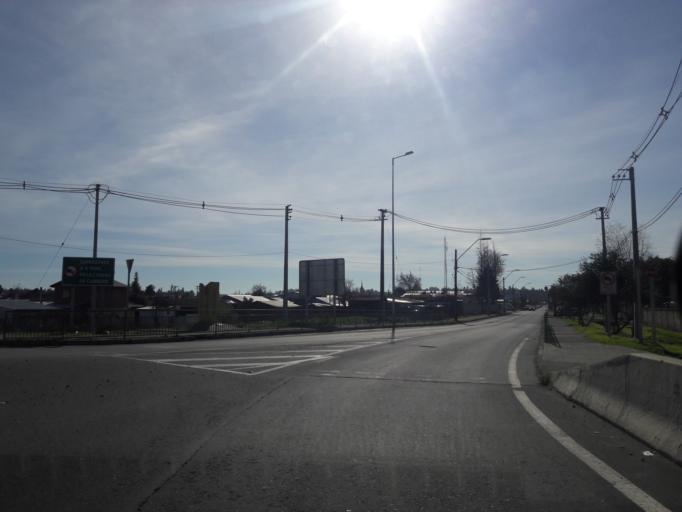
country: CL
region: Biobio
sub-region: Provincia de Biobio
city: Cabrero
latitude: -37.0394
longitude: -72.4048
